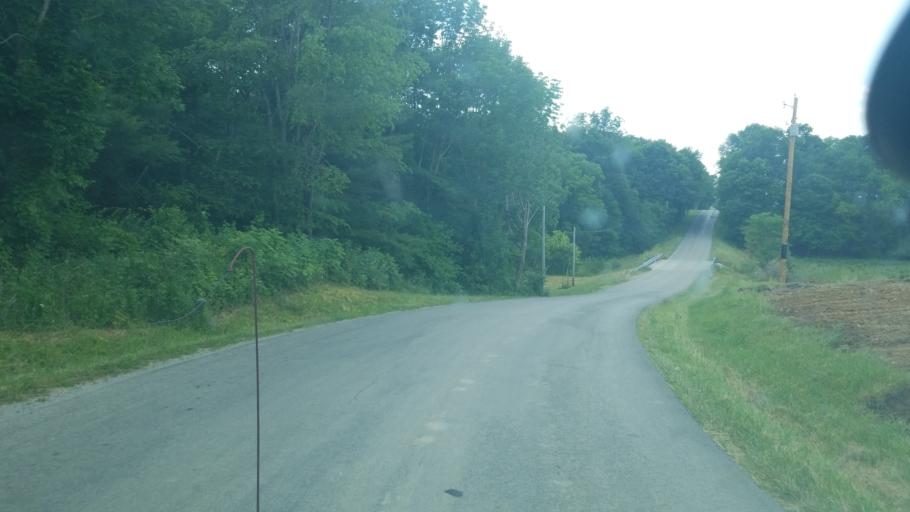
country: US
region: Ohio
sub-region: Highland County
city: Leesburg
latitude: 39.2952
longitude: -83.5703
